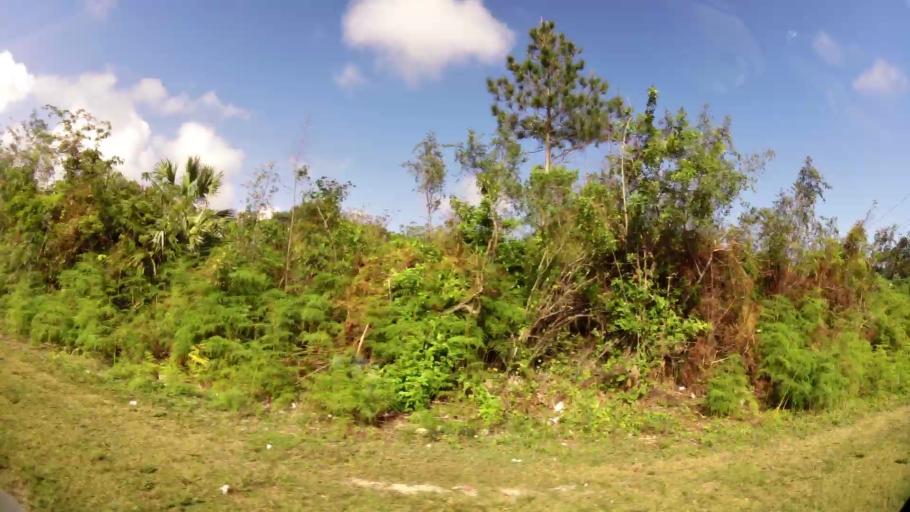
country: BS
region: Freeport
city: Lucaya
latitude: 26.5242
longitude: -78.6721
